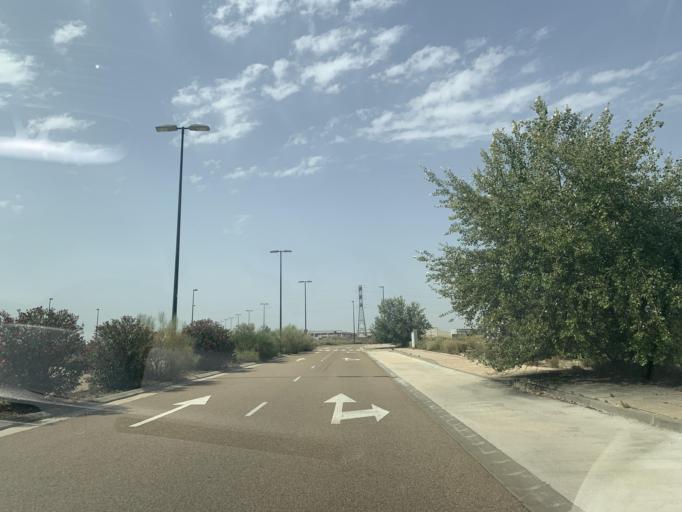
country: ES
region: Aragon
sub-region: Provincia de Zaragoza
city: El Burgo de Ebro
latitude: 41.5886
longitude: -0.8167
